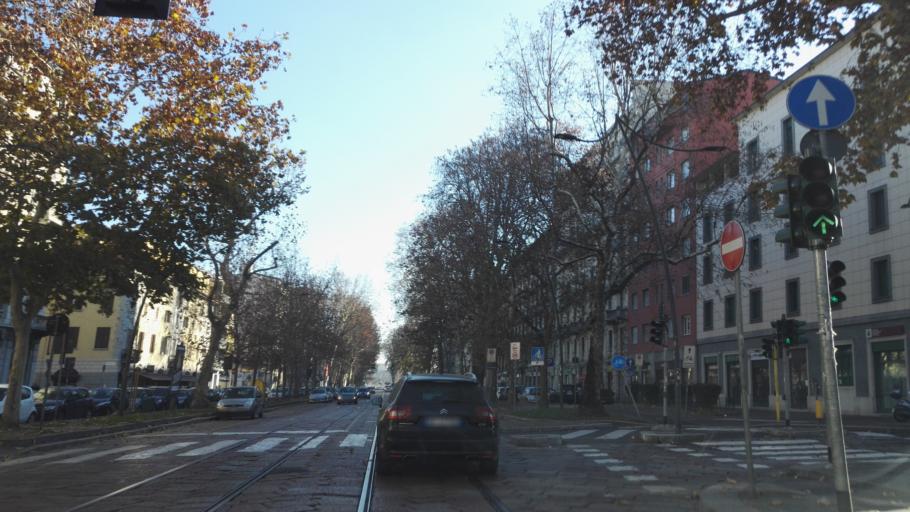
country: IT
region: Lombardy
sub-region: Citta metropolitana di Milano
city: Milano
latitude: 45.4495
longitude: 9.2065
